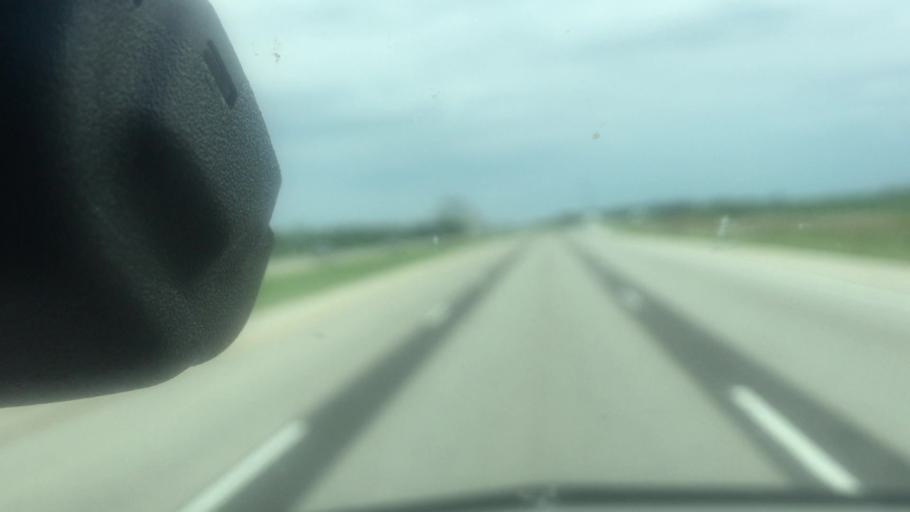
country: US
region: Illinois
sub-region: Sangamon County
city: Williamsville
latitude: 40.0310
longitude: -89.4759
